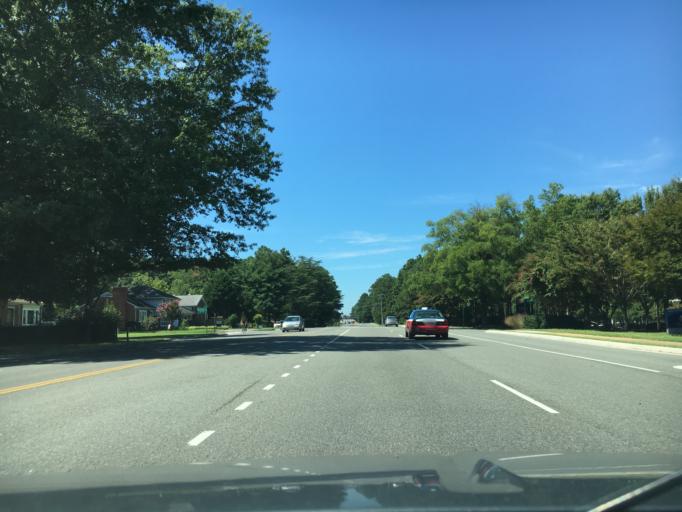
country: US
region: Virginia
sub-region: Henrico County
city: Tuckahoe
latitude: 37.5999
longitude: -77.5474
